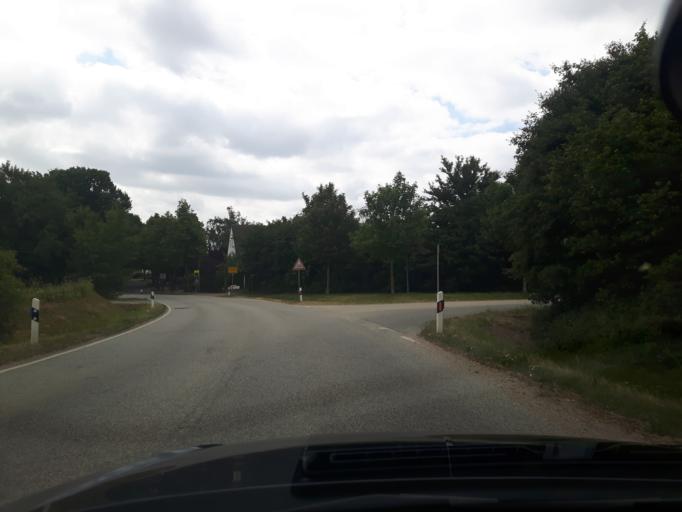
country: DE
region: Schleswig-Holstein
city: Neustadt in Holstein
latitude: 54.0959
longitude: 10.8538
